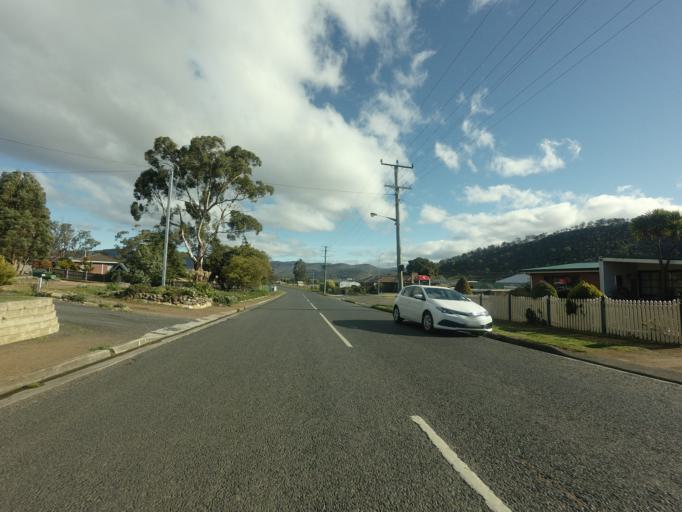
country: AU
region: Tasmania
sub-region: Derwent Valley
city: New Norfolk
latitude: -42.7572
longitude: 147.0497
